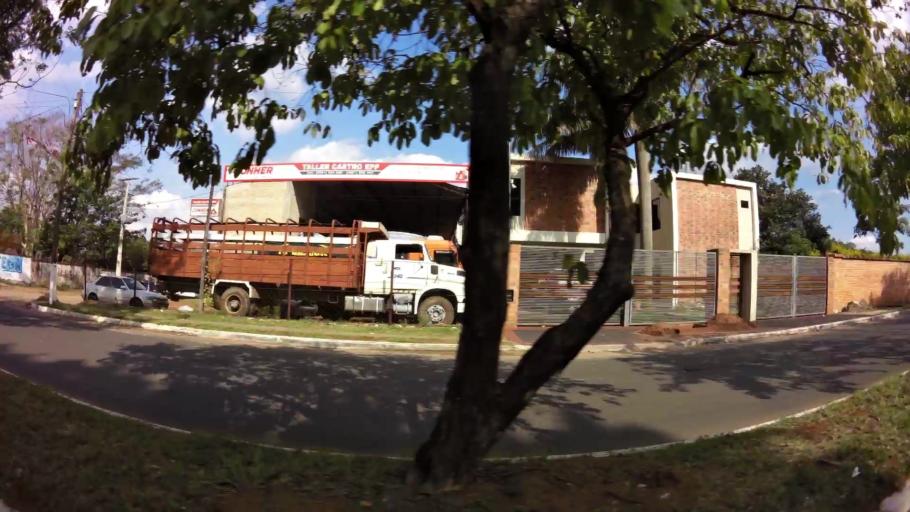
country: PY
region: Central
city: Fernando de la Mora
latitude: -25.3429
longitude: -57.5409
